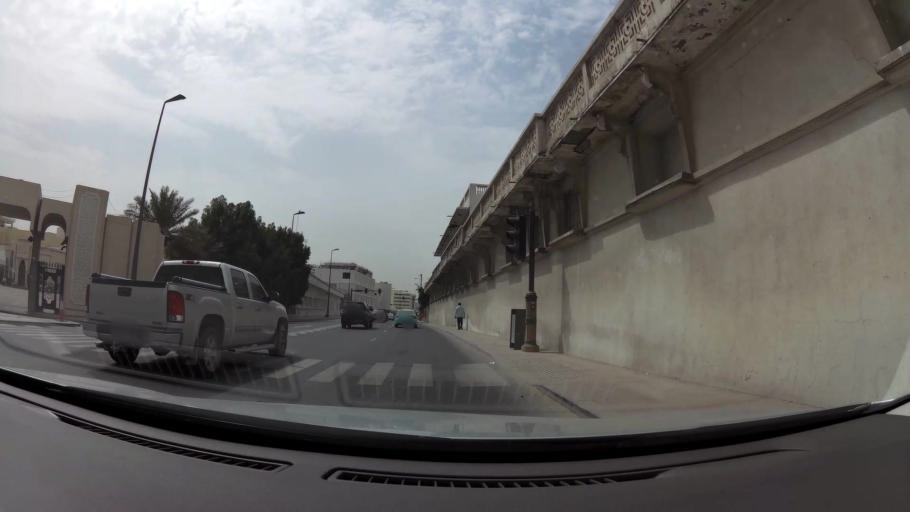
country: QA
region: Baladiyat ad Dawhah
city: Doha
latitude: 25.2884
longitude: 51.5266
